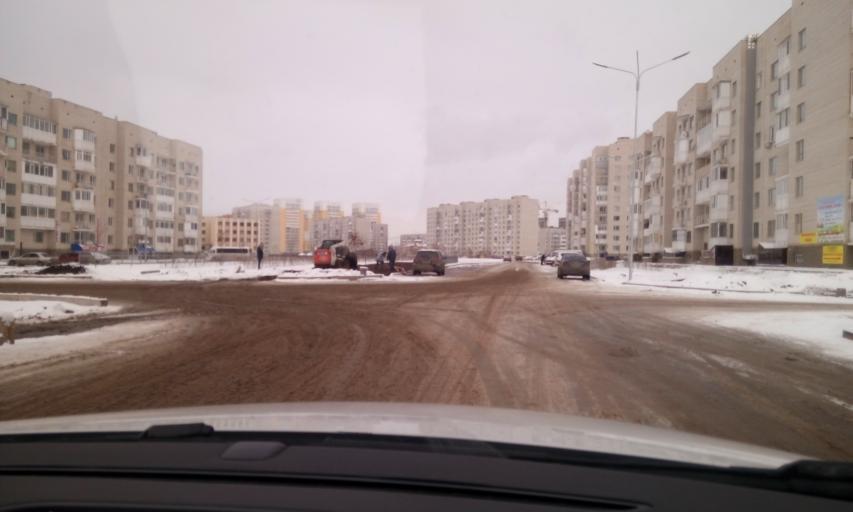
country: KZ
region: Astana Qalasy
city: Astana
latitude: 51.1221
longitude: 71.5043
